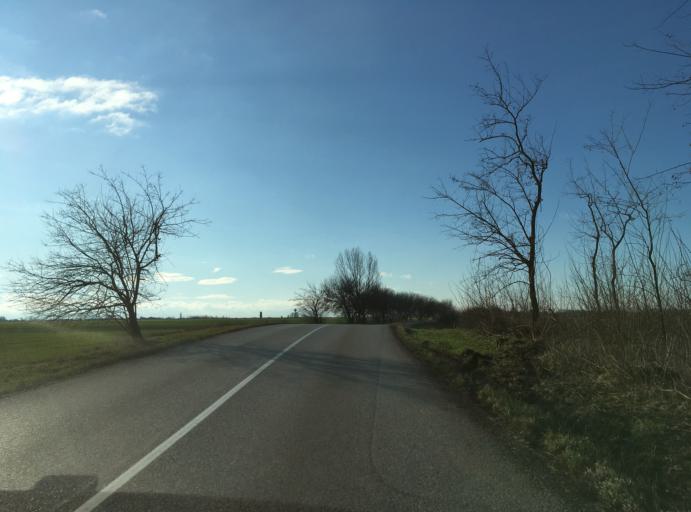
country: SK
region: Nitriansky
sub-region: Okres Komarno
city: Hurbanovo
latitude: 47.8252
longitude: 18.2336
